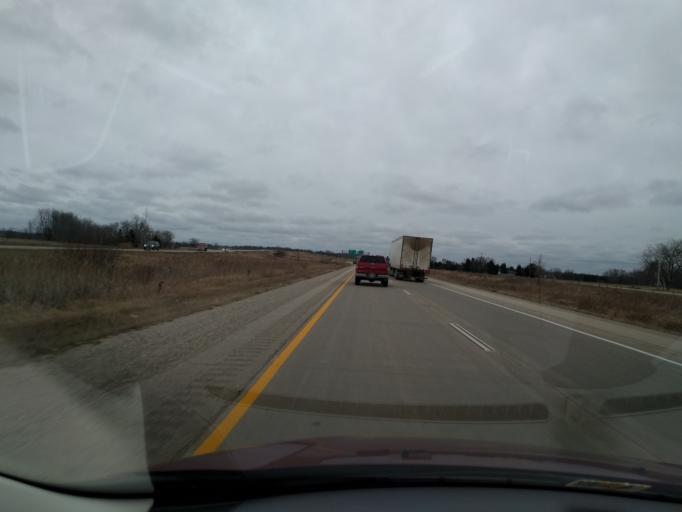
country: US
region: Wisconsin
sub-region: Winnebago County
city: Winneconne
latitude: 44.2123
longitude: -88.6920
